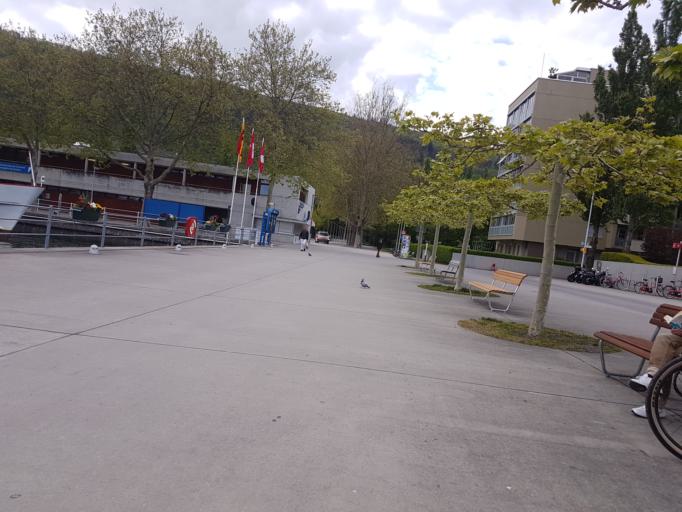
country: CH
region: Bern
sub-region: Biel/Bienne District
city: Nidau
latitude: 47.1309
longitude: 7.2361
